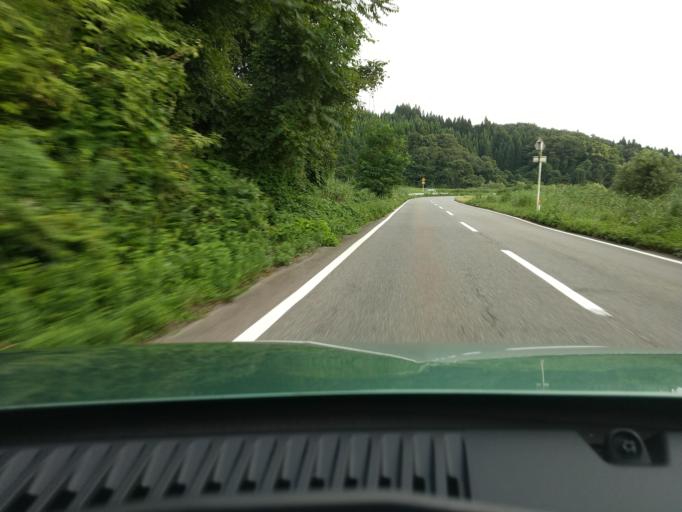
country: JP
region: Akita
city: Akita
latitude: 39.7489
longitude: 140.1609
